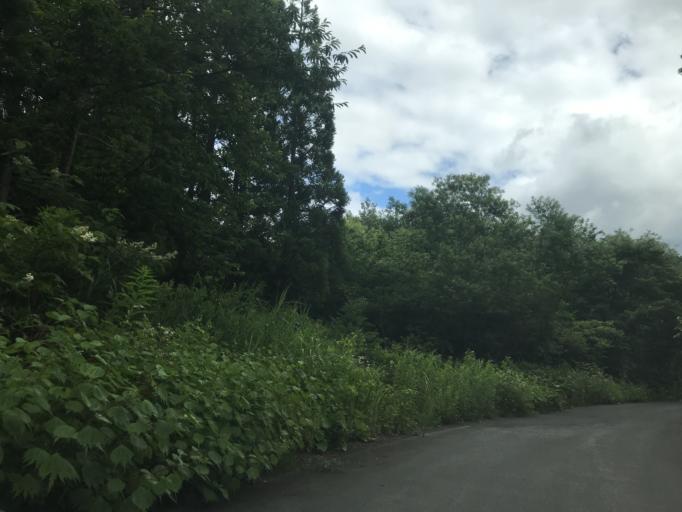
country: JP
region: Iwate
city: Ichinoseki
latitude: 38.9596
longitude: 140.8940
